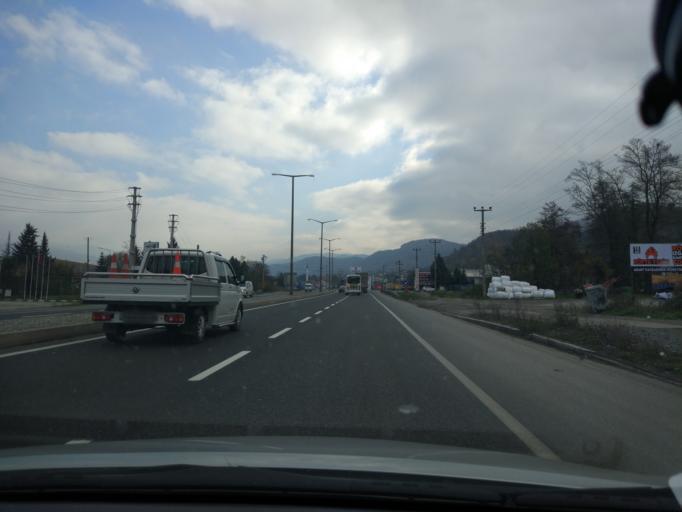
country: TR
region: Duzce
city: Kaynasli
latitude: 40.7804
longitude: 31.2817
